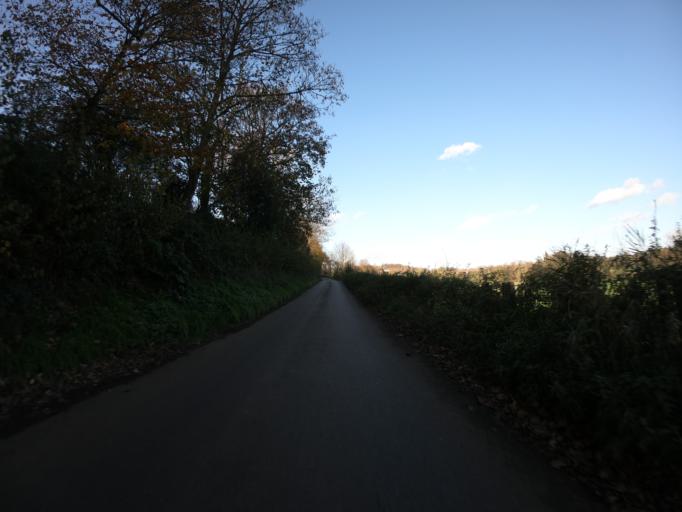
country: GB
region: England
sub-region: Kent
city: Eynsford
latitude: 51.3648
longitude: 0.1969
